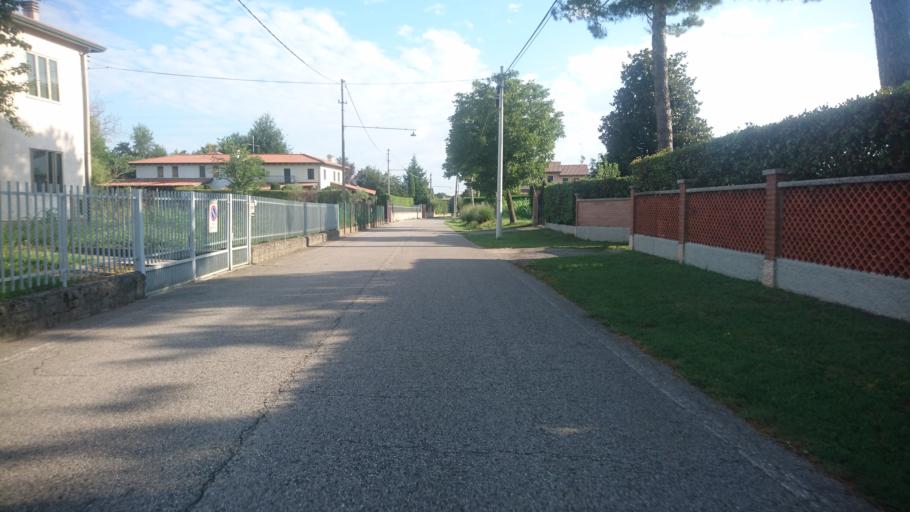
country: IT
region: Veneto
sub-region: Provincia di Padova
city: Sarmeola
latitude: 45.4218
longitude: 11.8318
